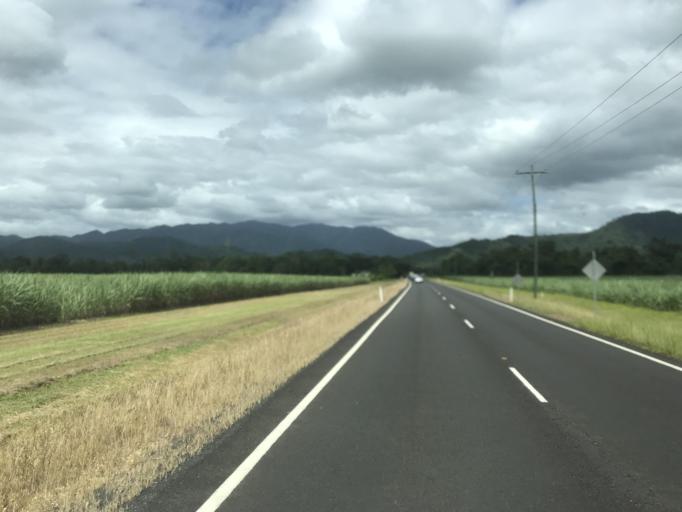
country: AU
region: Queensland
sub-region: Cassowary Coast
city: Innisfail
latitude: -17.8100
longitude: 146.0157
